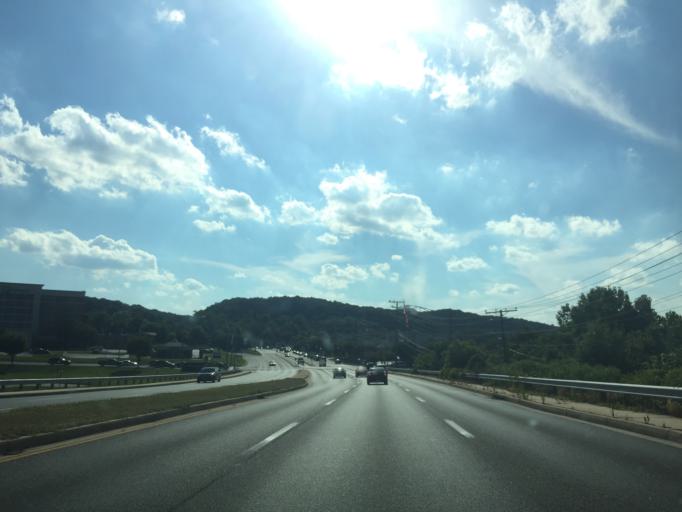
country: US
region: Maryland
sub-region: Baltimore County
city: Mays Chapel
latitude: 39.4556
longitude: -76.6401
